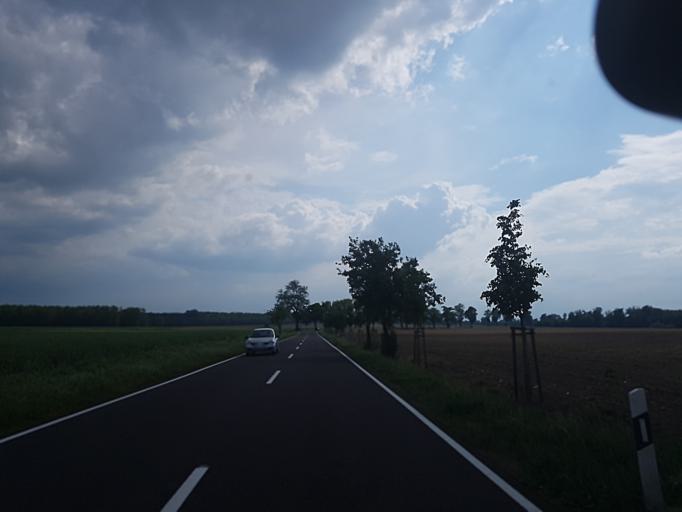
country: DE
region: Saxony-Anhalt
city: Lindau
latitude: 52.0367
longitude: 12.2515
